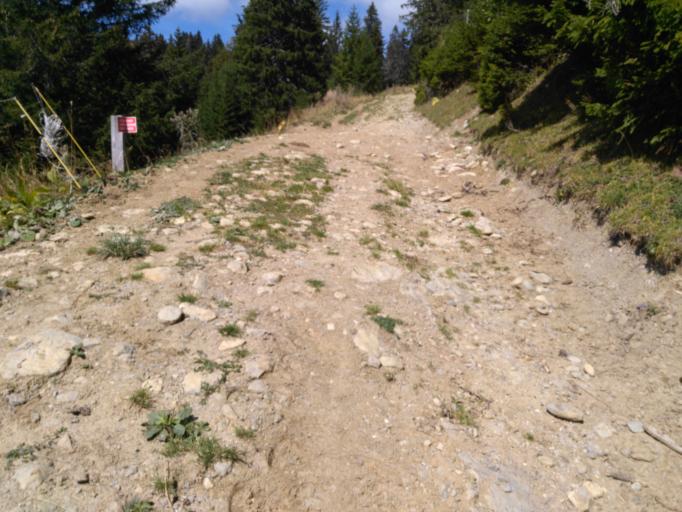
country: FR
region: Rhone-Alpes
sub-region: Departement de la Haute-Savoie
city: Viuz-la-Chiesaz
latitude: 45.7862
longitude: 6.1063
